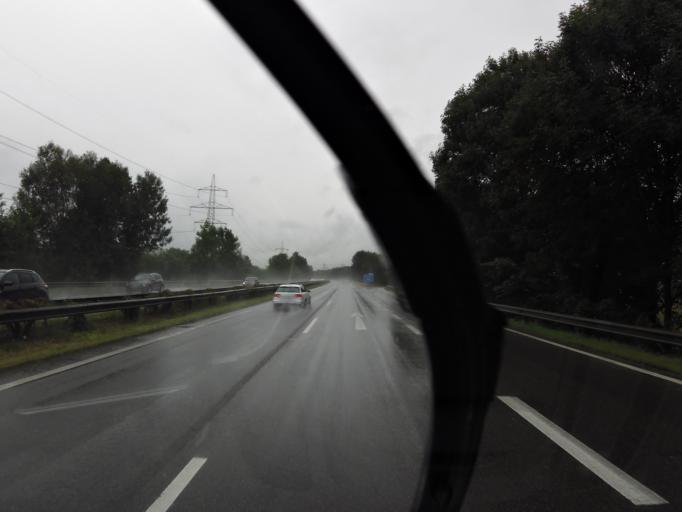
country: AT
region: Vorarlberg
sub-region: Politischer Bezirk Dornbirn
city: Hohenems
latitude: 47.3727
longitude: 9.6674
